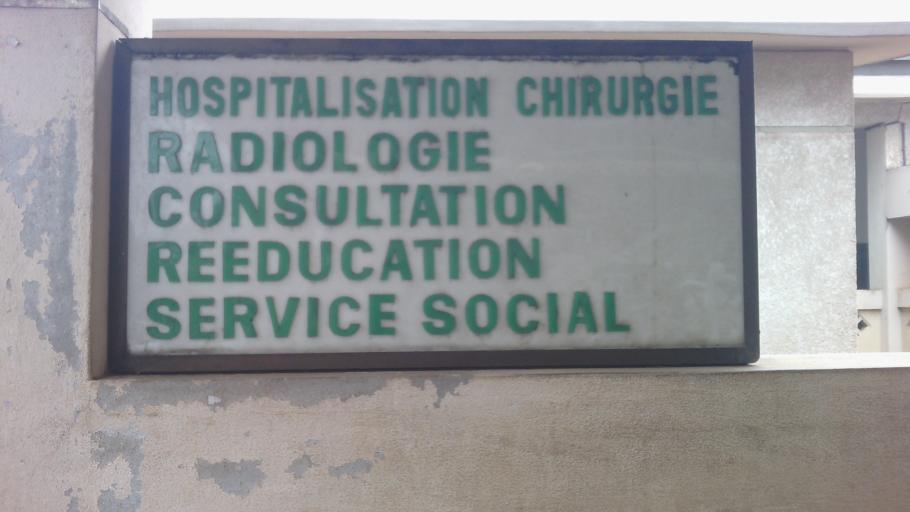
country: BJ
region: Queme
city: Porto-Novo
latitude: 6.4737
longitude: 2.6142
